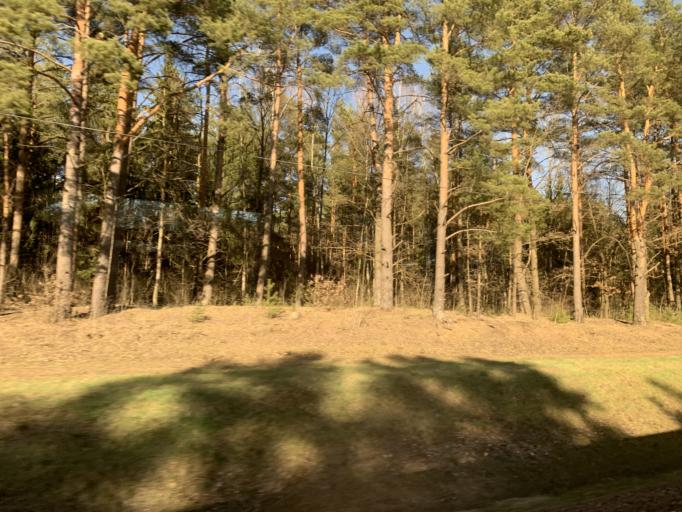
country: BY
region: Grodnenskaya
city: Astravyets
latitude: 54.5771
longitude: 25.9382
